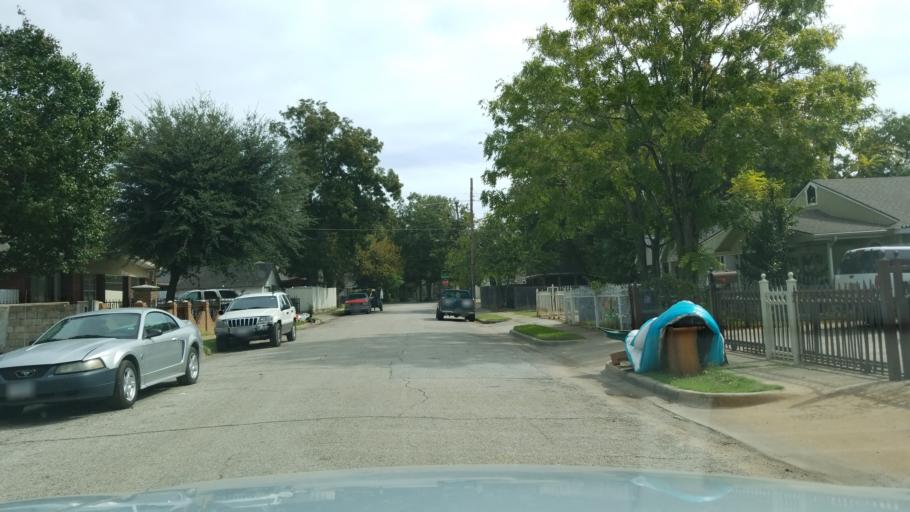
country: US
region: Texas
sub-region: Dallas County
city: Dallas
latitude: 32.7891
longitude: -96.7455
